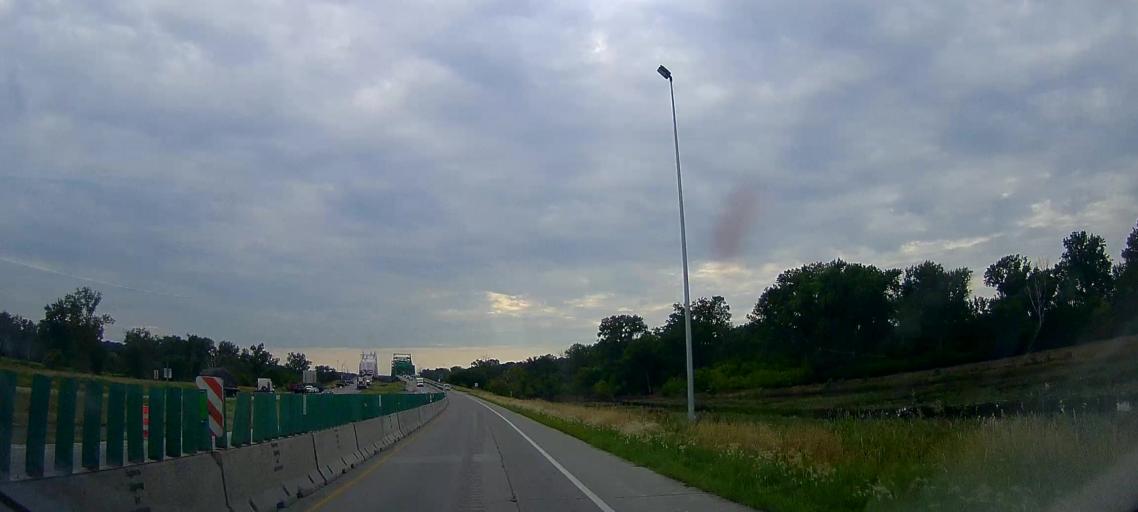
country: US
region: Iowa
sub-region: Pottawattamie County
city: Carter Lake
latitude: 41.3468
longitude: -95.9505
